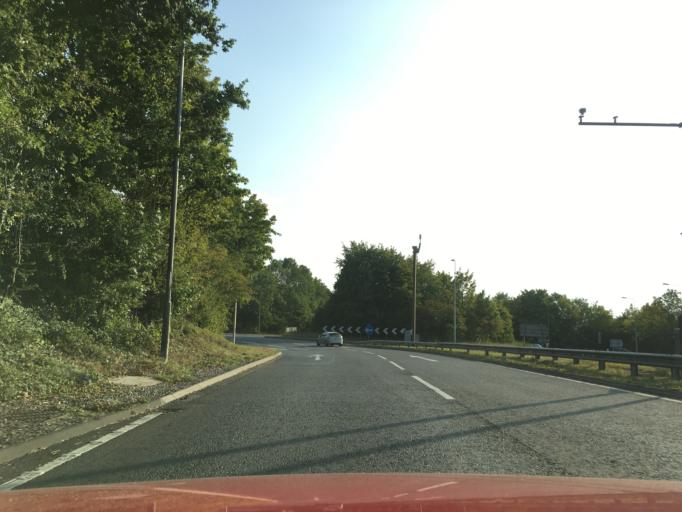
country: GB
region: Wales
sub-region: Torfaen County Borough
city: Cwmbran
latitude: 51.6511
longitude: -3.0005
